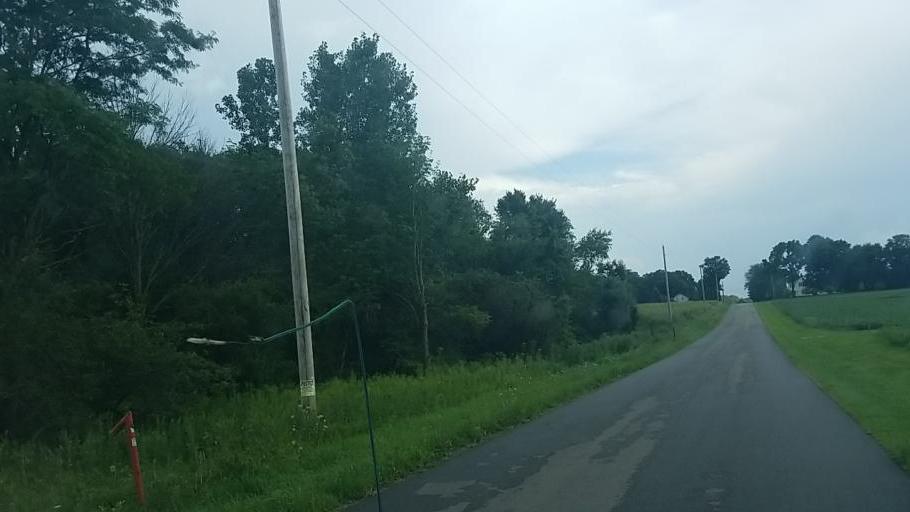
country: US
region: Ohio
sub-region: Wayne County
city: Creston
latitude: 40.9559
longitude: -81.9377
